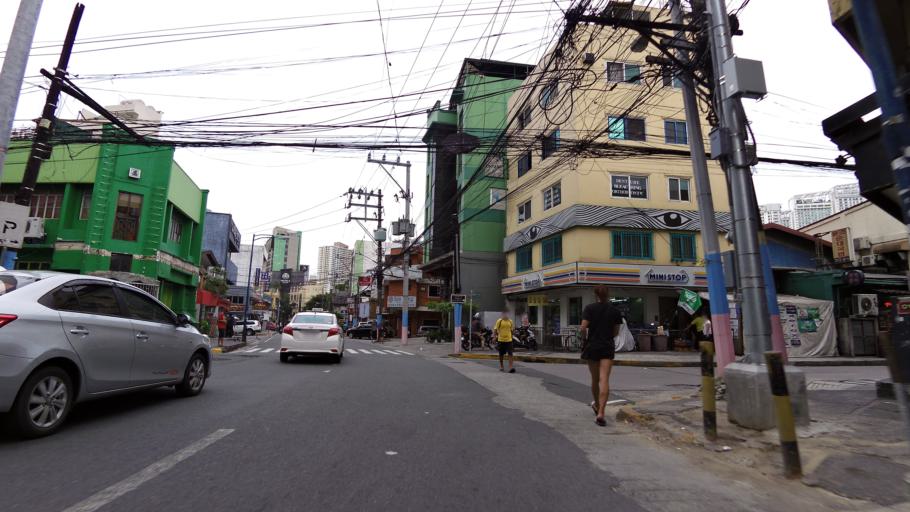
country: PH
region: Metro Manila
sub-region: Makati City
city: Makati City
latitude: 14.5646
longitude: 121.0310
